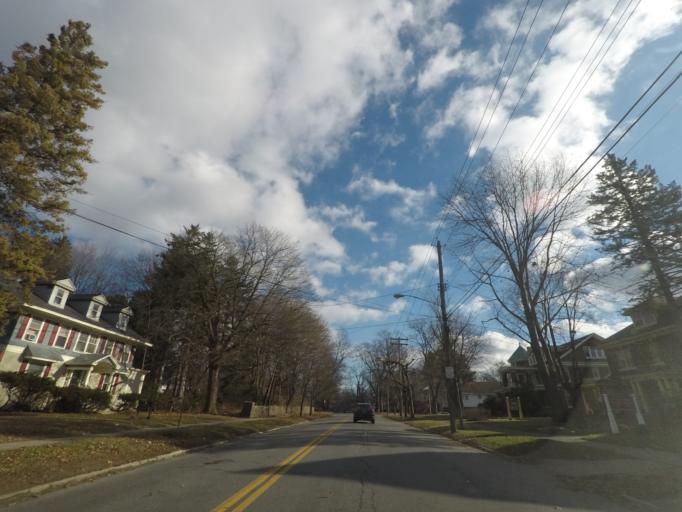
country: US
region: New York
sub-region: Schenectady County
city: Schenectady
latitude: 42.8100
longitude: -73.9188
